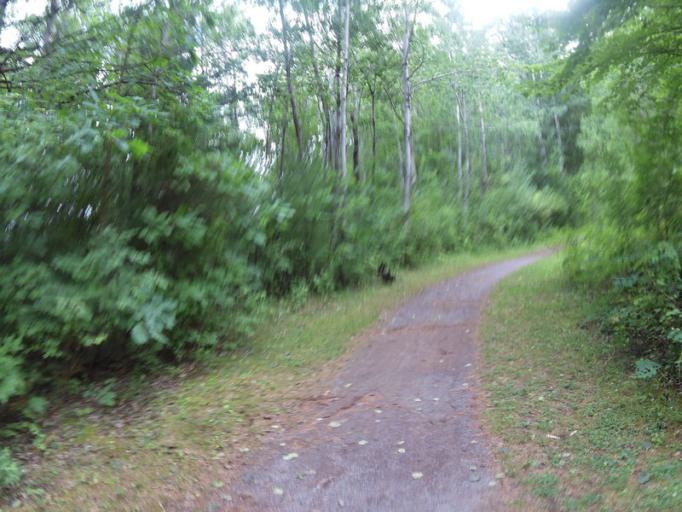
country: CA
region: Ontario
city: Bells Corners
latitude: 45.3276
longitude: -75.7406
